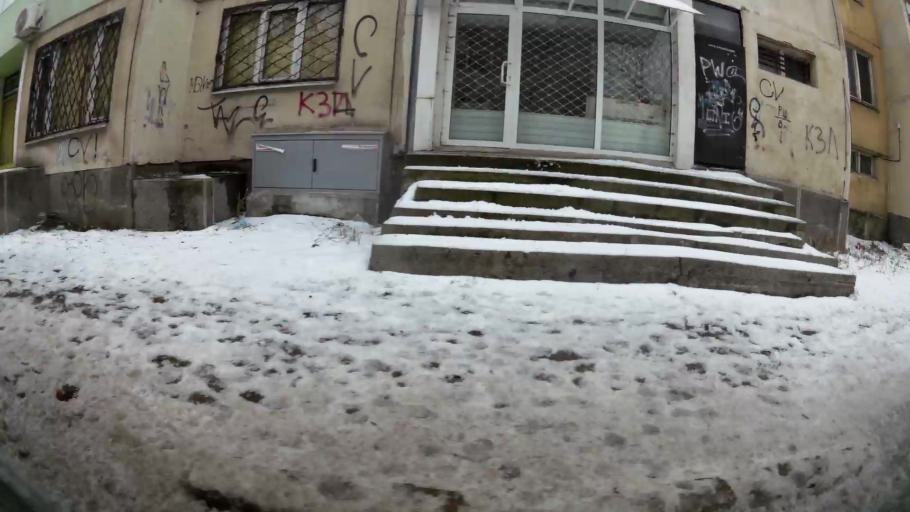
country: BG
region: Sofia-Capital
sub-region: Stolichna Obshtina
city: Sofia
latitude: 42.7112
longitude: 23.2969
